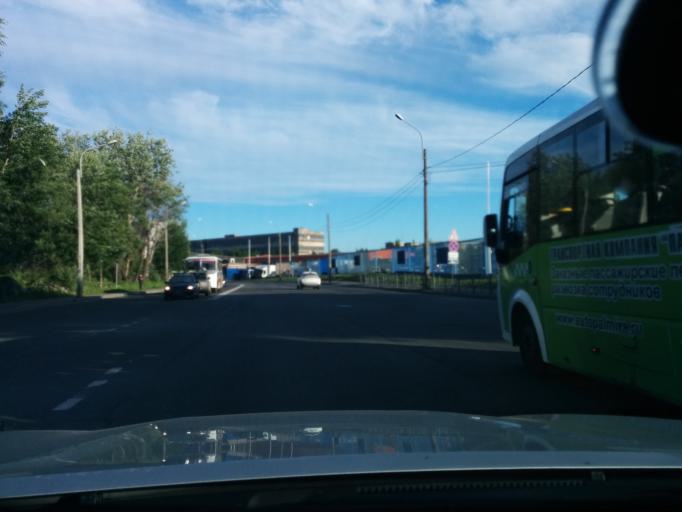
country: RU
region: Leningrad
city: Finlyandskiy
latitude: 59.9778
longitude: 30.3674
